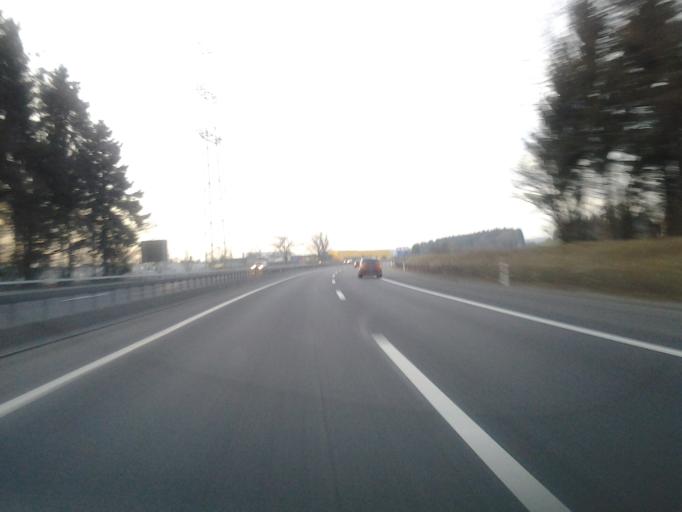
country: CH
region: Lucerne
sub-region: Hochdorf District
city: Emmen
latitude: 47.0923
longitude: 8.2477
